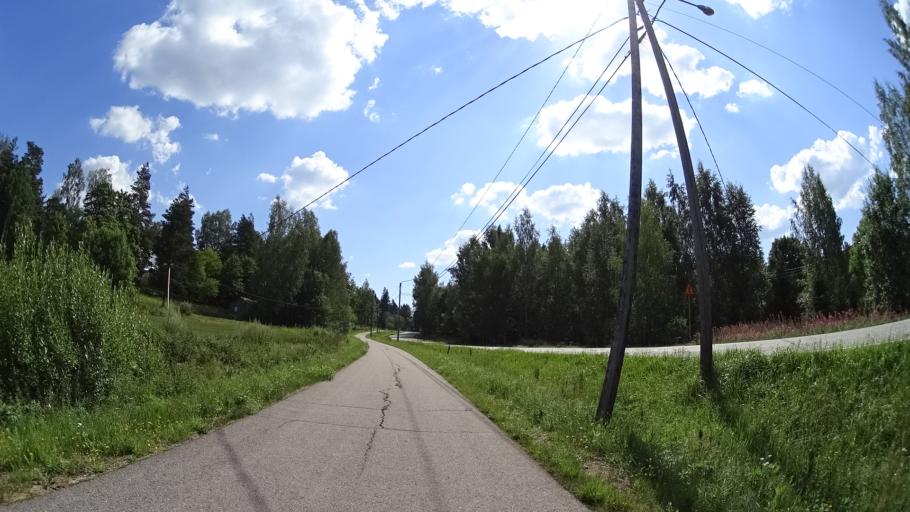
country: FI
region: Uusimaa
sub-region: Helsinki
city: Tuusula
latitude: 60.3663
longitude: 24.9800
